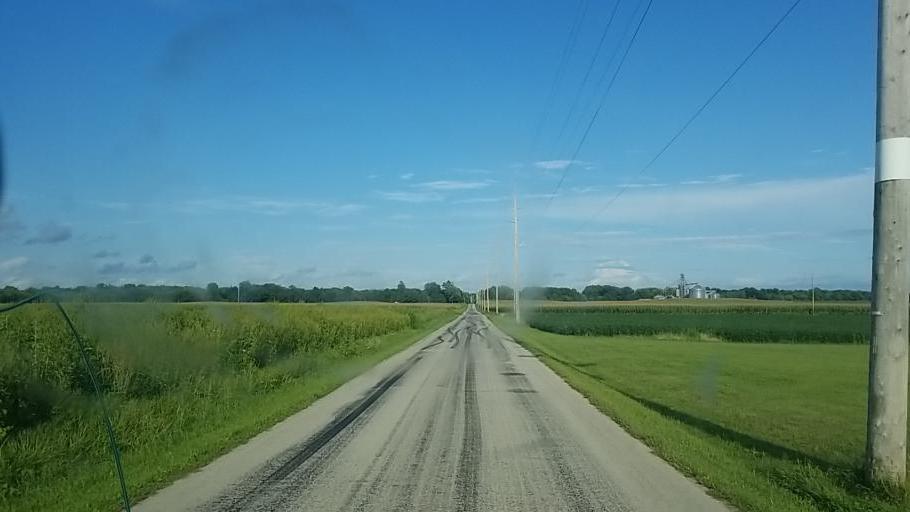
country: US
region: Ohio
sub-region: Wyandot County
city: Upper Sandusky
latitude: 40.8147
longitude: -83.1615
